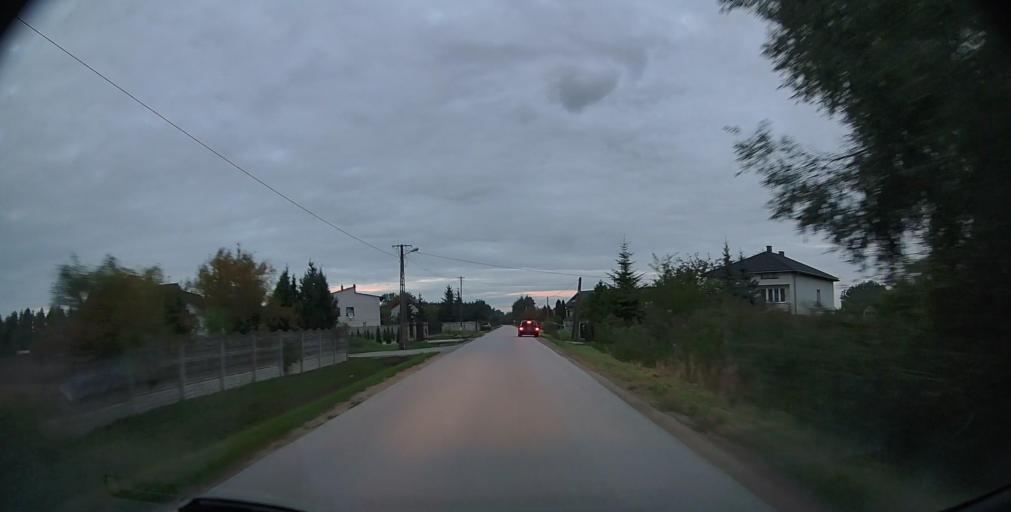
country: PL
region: Masovian Voivodeship
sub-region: Powiat radomski
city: Jedlinsk
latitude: 51.4613
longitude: 21.1247
